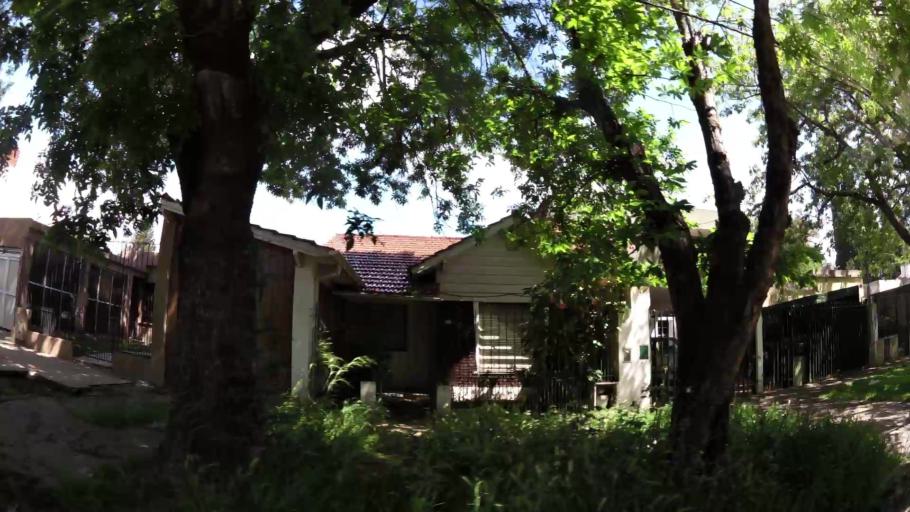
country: AR
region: Buenos Aires
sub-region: Partido de Quilmes
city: Quilmes
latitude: -34.8127
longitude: -58.2714
